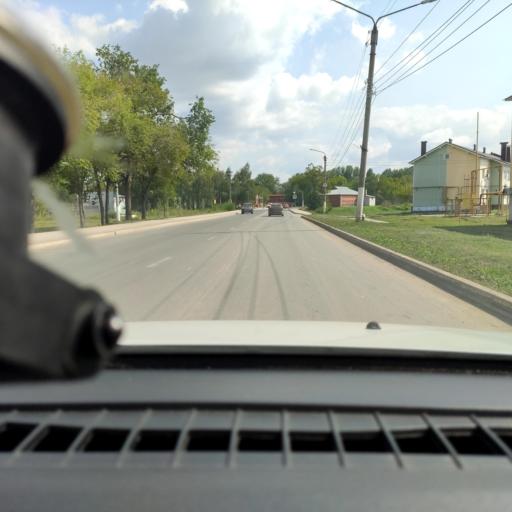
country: RU
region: Samara
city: Chapayevsk
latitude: 52.9852
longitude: 49.7068
